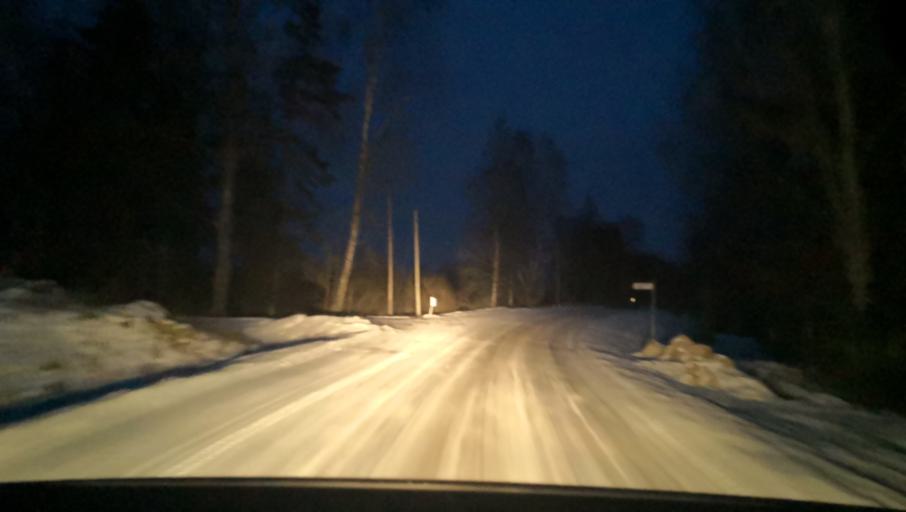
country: SE
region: Uppsala
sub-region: Heby Kommun
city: Tarnsjo
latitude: 60.2622
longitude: 16.7830
